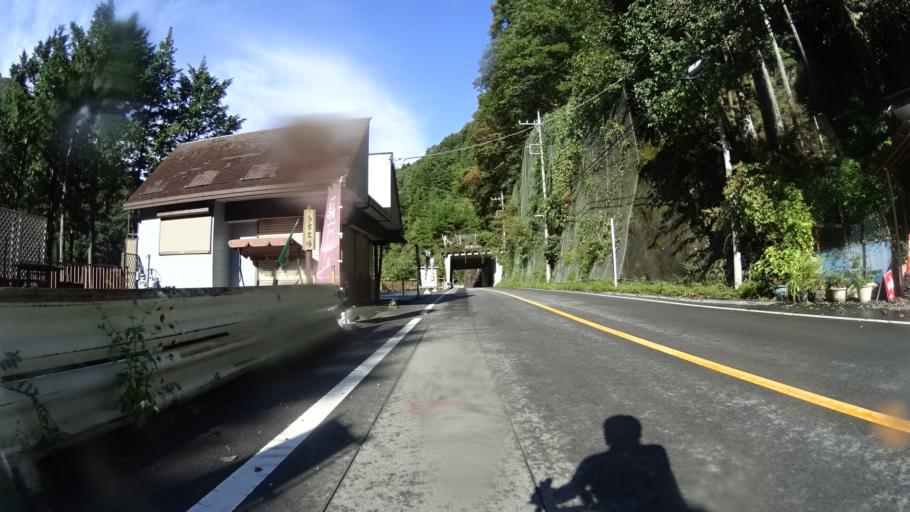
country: JP
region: Yamanashi
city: Otsuki
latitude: 35.7885
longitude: 138.9435
